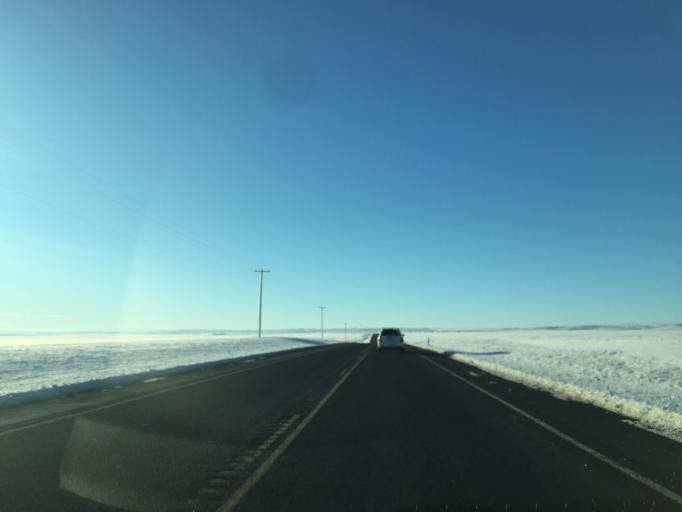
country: US
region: Washington
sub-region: Okanogan County
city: Coulee Dam
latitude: 47.6845
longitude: -119.0278
